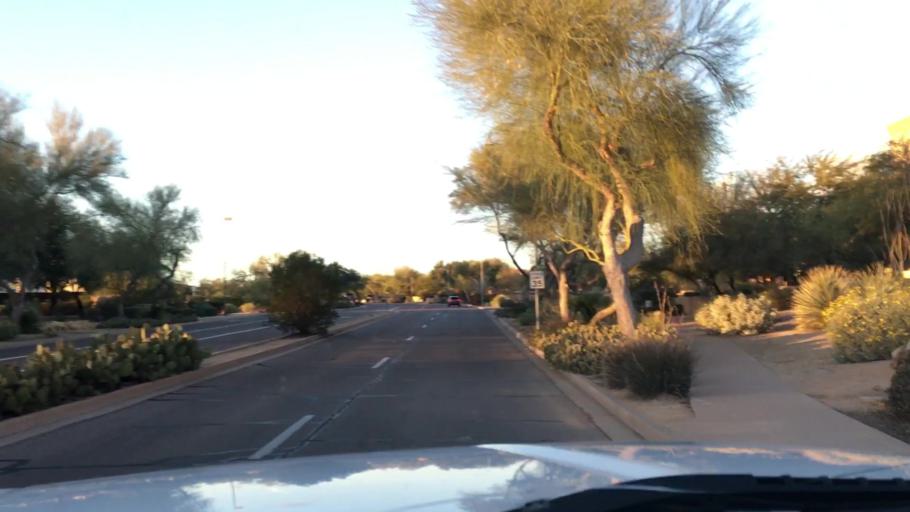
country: US
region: Arizona
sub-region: Maricopa County
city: Paradise Valley
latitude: 33.6410
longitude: -111.8960
